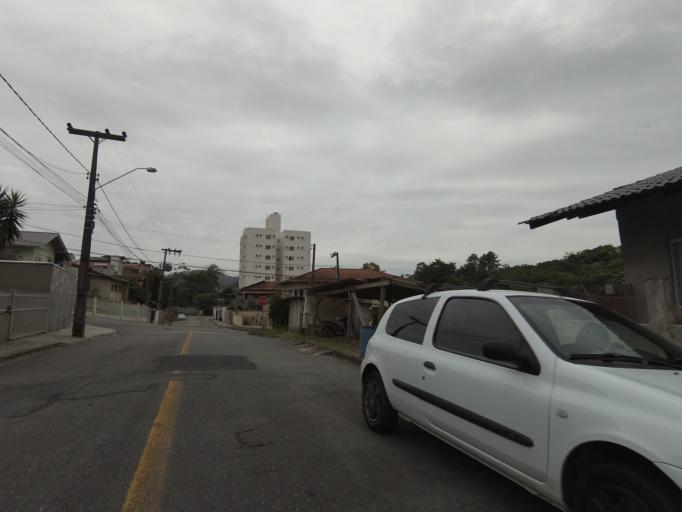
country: BR
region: Santa Catarina
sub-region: Blumenau
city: Blumenau
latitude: -26.8999
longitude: -49.1276
